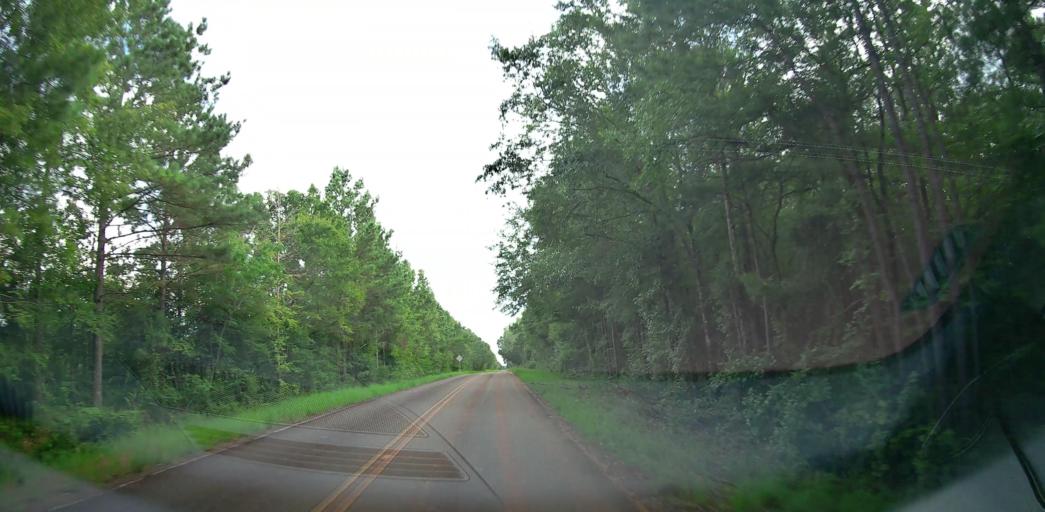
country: US
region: Georgia
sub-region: Bleckley County
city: Cochran
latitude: 32.4476
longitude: -83.4494
